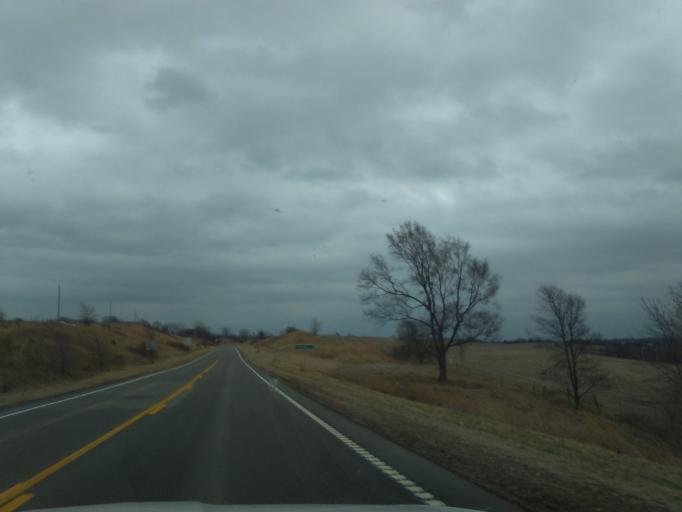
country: US
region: Nebraska
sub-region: Nemaha County
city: Auburn
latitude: 40.4652
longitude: -95.7331
